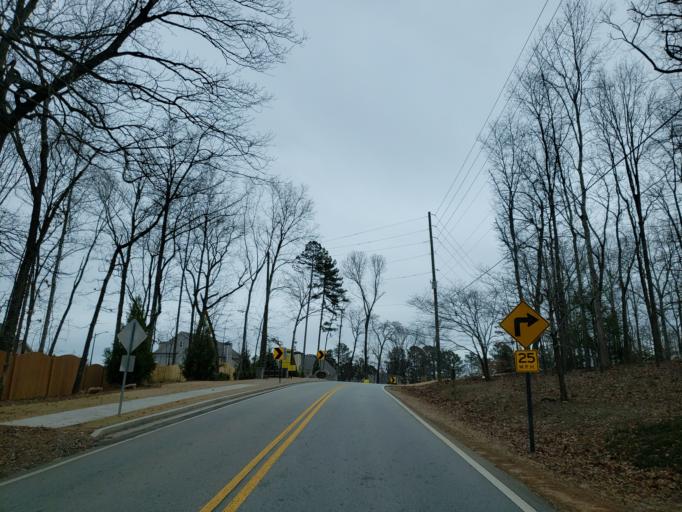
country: US
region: Georgia
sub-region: Paulding County
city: Hiram
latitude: 33.9235
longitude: -84.7231
